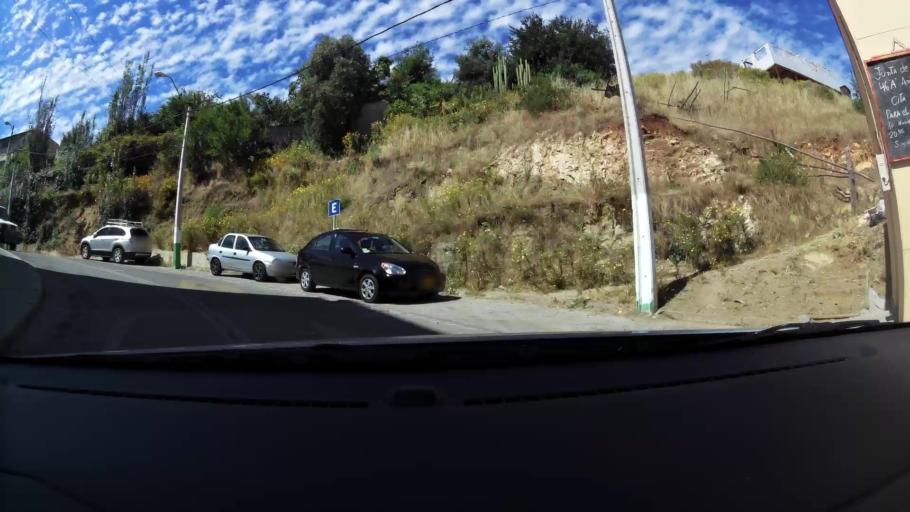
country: CL
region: Valparaiso
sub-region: Provincia de Valparaiso
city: Vina del Mar
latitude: -33.0431
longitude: -71.5784
